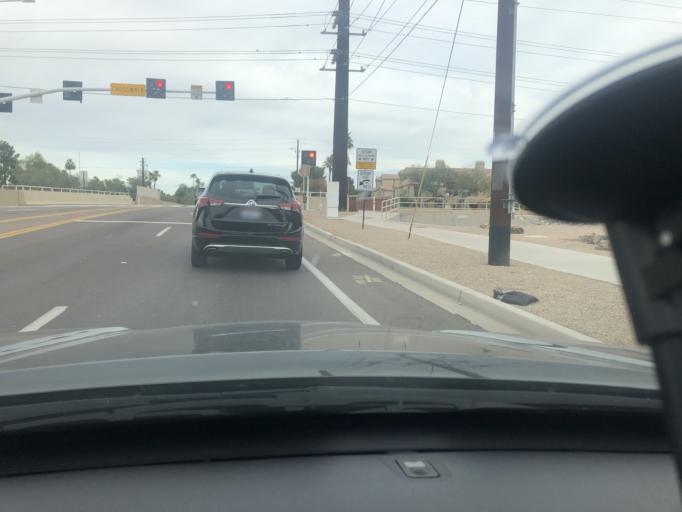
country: US
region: Arizona
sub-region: Maricopa County
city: Scottsdale
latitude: 33.5240
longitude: -111.9163
